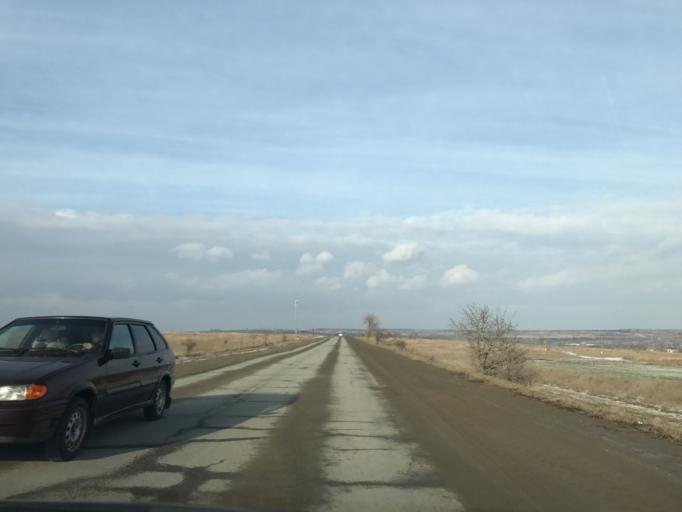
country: RU
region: Rostov
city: Staraya Stanitsa
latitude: 48.2778
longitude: 40.3452
